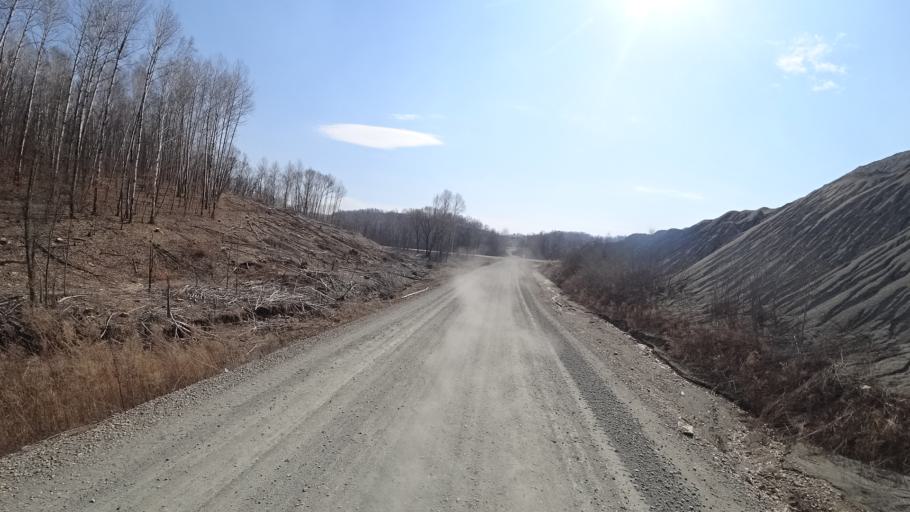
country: RU
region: Amur
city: Novobureyskiy
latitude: 49.7980
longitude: 129.9579
